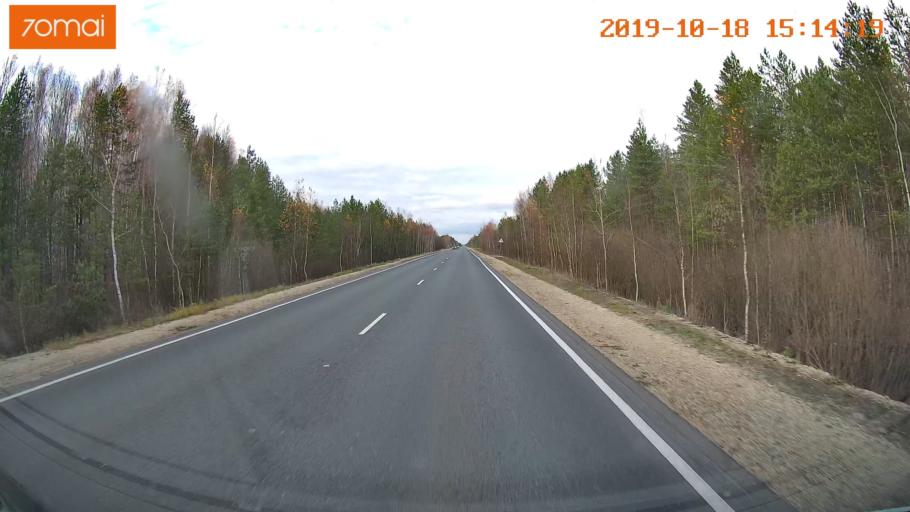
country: RU
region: Vladimir
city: Gus'-Khrustal'nyy
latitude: 55.6006
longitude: 40.7200
